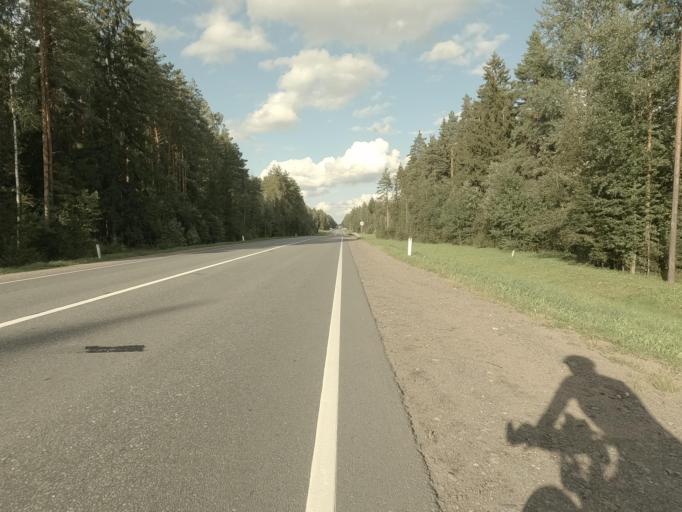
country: RU
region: Leningrad
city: Mga
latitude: 59.6926
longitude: 30.9791
